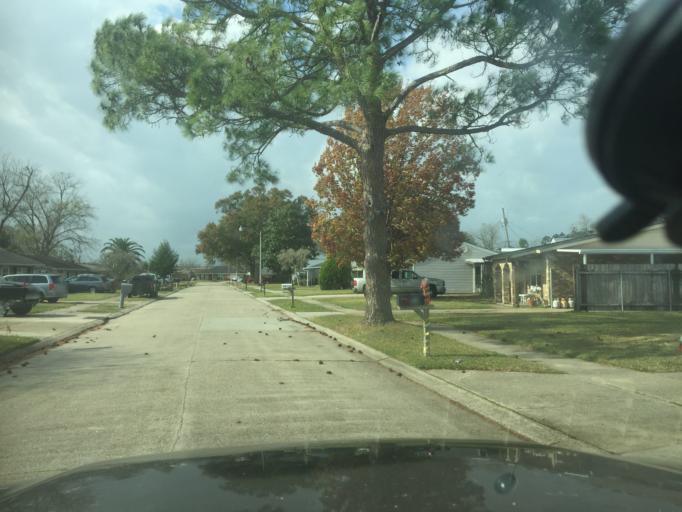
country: US
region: Louisiana
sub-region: Jefferson Parish
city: Avondale
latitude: 29.9120
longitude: -90.2045
